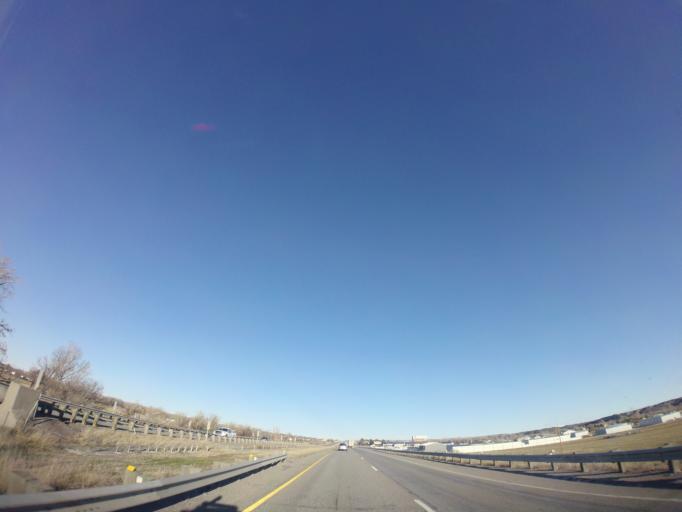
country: US
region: Montana
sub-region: Yellowstone County
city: Laurel
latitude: 45.7055
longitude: -108.6582
